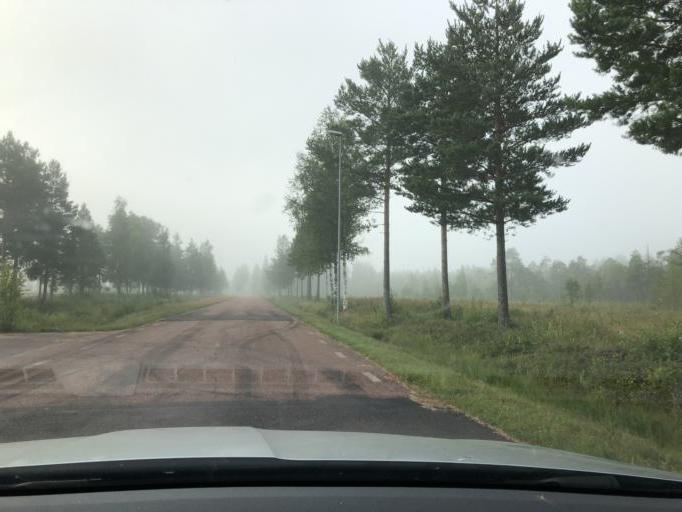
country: SE
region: Dalarna
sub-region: Mora Kommun
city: Mora
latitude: 60.9624
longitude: 14.5005
